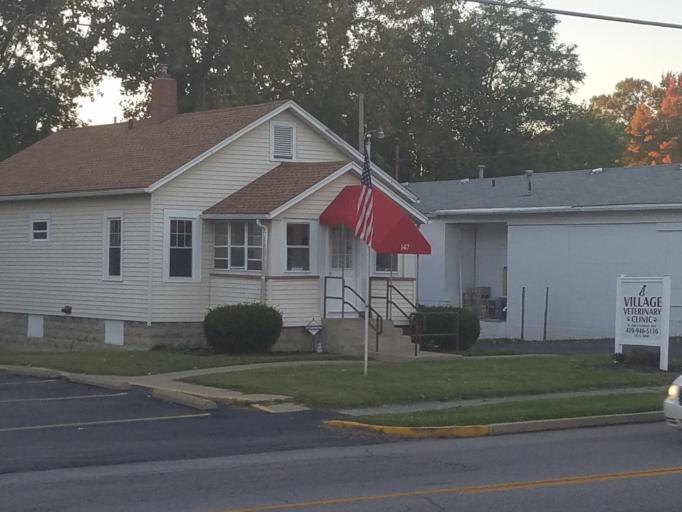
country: US
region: Ohio
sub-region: Morrow County
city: Mount Gilead
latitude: 40.5456
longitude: -82.8296
